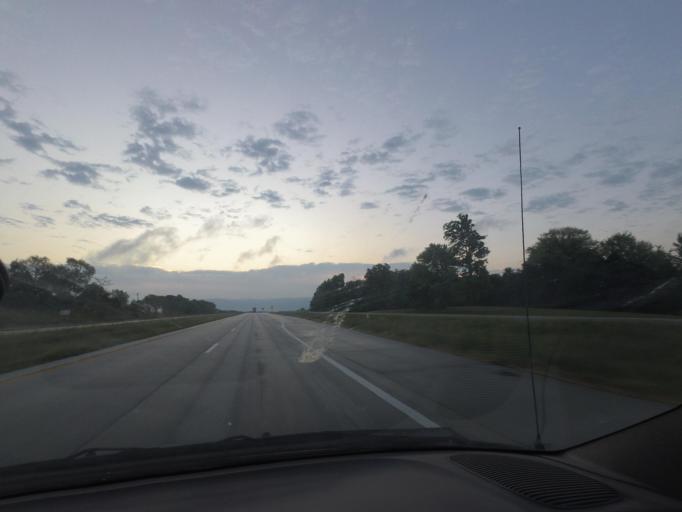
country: US
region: Missouri
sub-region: Macon County
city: Macon
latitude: 39.7488
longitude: -92.5117
